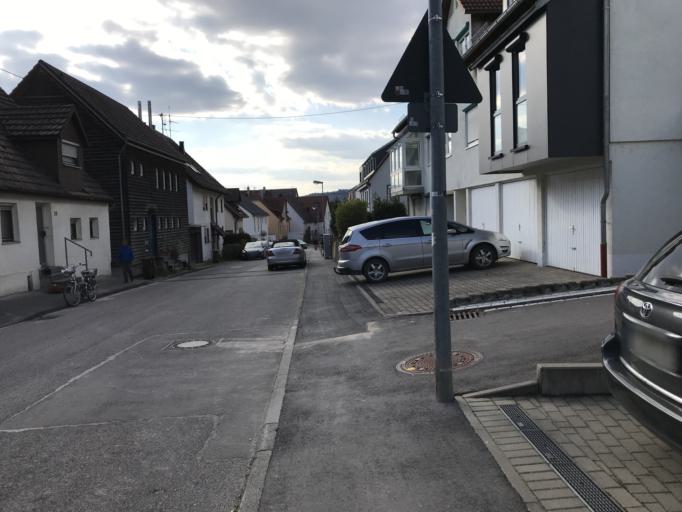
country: DE
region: Baden-Wuerttemberg
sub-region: Regierungsbezirk Stuttgart
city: Oberboihingen
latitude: 48.6488
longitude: 9.3687
